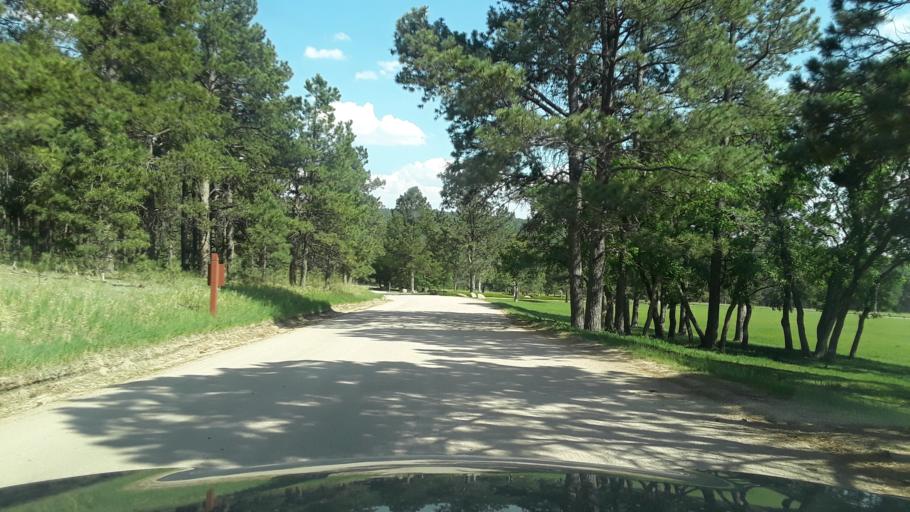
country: US
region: Colorado
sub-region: El Paso County
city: Gleneagle
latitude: 39.0580
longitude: -104.7913
